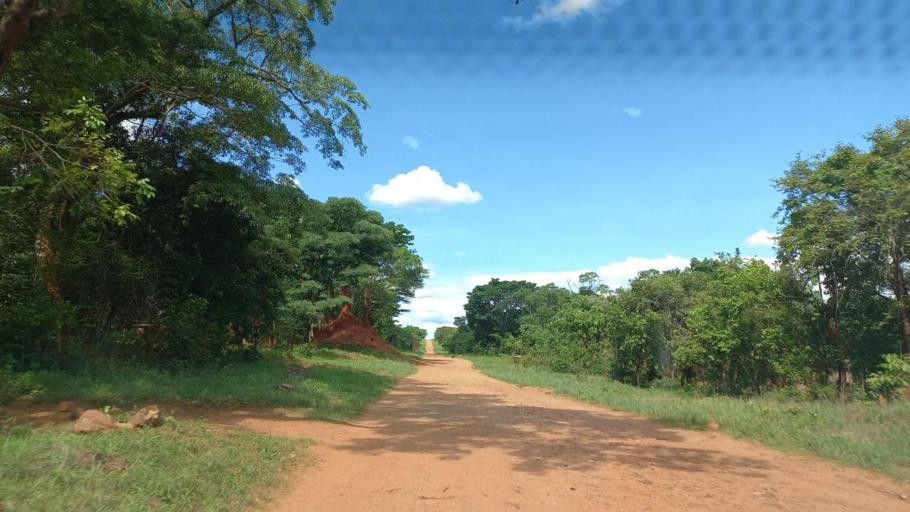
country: ZM
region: North-Western
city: Mwinilunga
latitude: -12.1161
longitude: 24.2802
